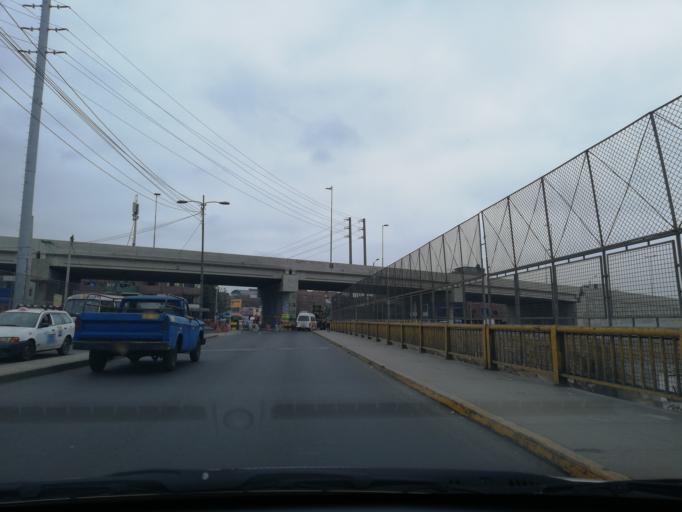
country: PE
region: Lima
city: Lima
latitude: -12.0347
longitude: -77.0655
